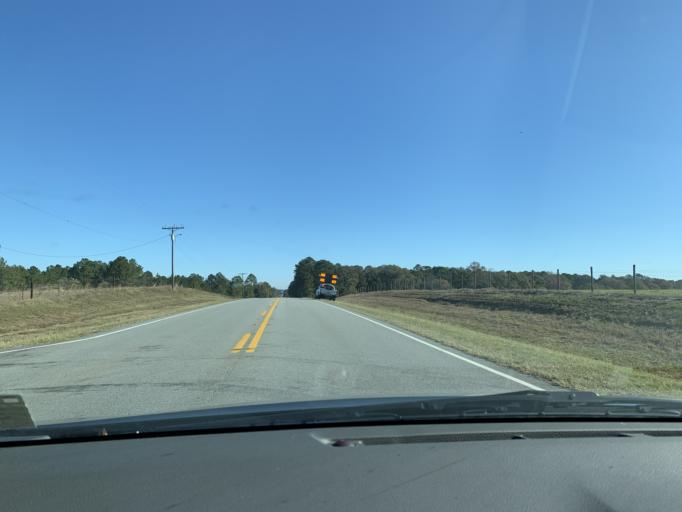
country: US
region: Georgia
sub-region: Ben Hill County
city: Fitzgerald
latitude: 31.7453
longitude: -83.1466
